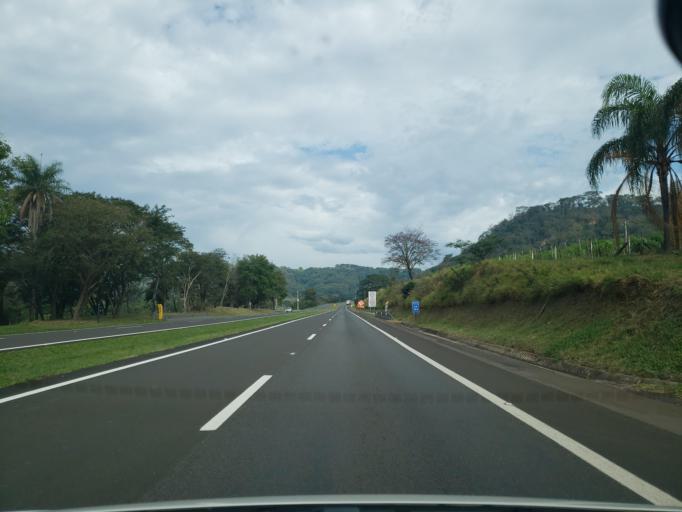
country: BR
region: Sao Paulo
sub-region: Dois Corregos
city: Dois Corregos
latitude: -22.2472
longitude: -48.3314
